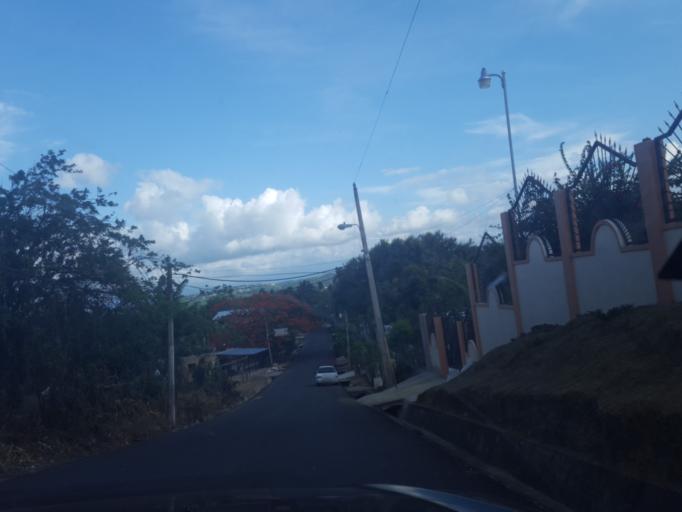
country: DO
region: La Vega
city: Rio Verde Arriba
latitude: 19.3503
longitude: -70.6265
